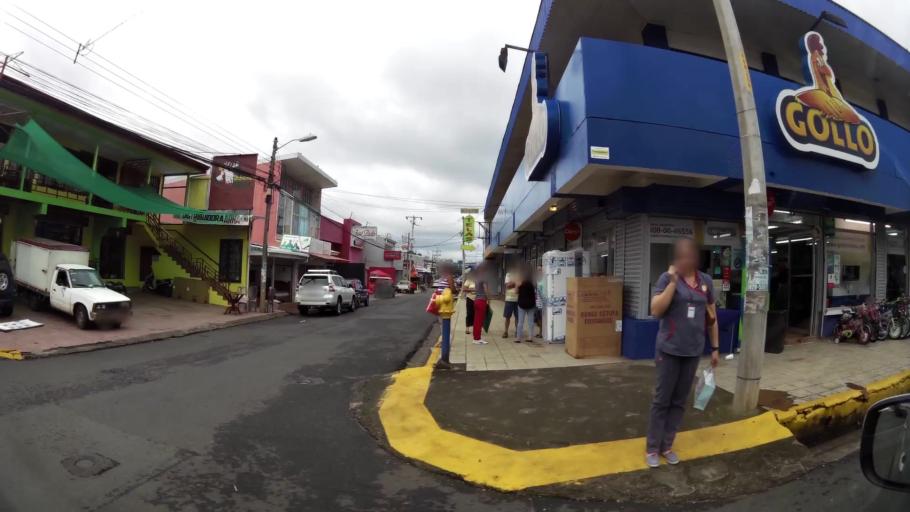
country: CR
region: Puntarenas
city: Esparza
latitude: 9.9914
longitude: -84.6666
